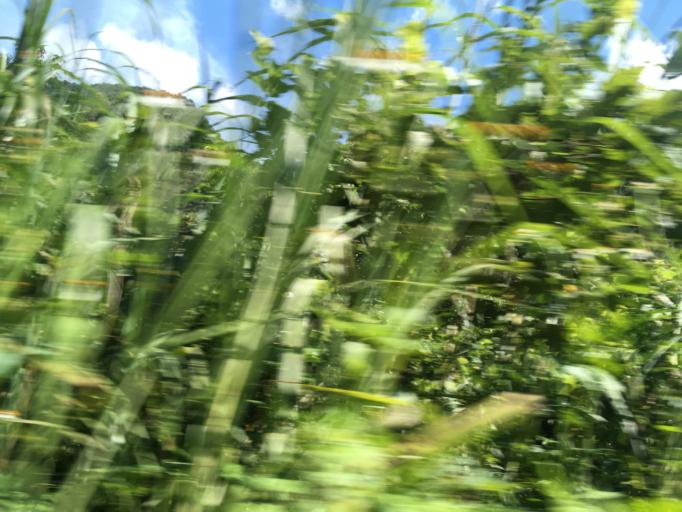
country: TW
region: Taiwan
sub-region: Yilan
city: Yilan
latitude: 24.4241
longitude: 121.7150
